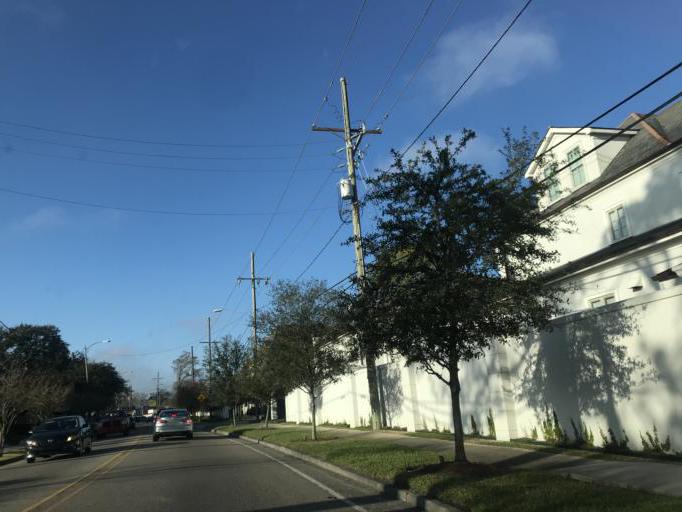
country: US
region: Louisiana
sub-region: Jefferson Parish
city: Metairie
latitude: 29.9848
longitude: -90.1474
